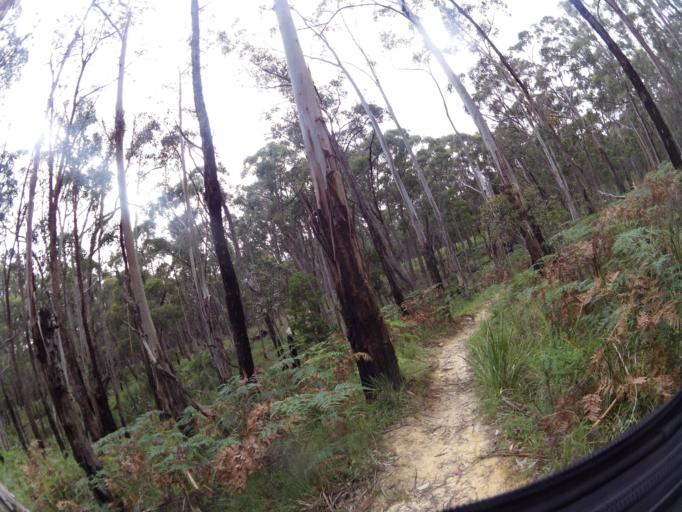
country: AU
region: Victoria
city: Brown Hill
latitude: -37.4855
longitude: 143.9114
